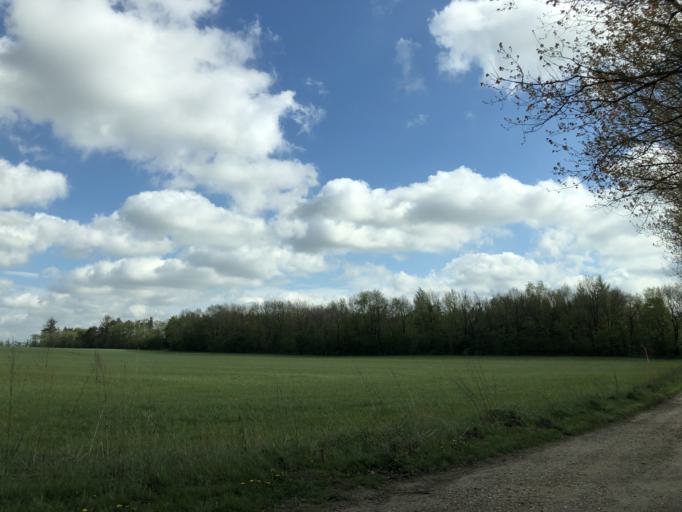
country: DK
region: Central Jutland
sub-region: Herning Kommune
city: Avlum
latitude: 56.3031
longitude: 8.7648
